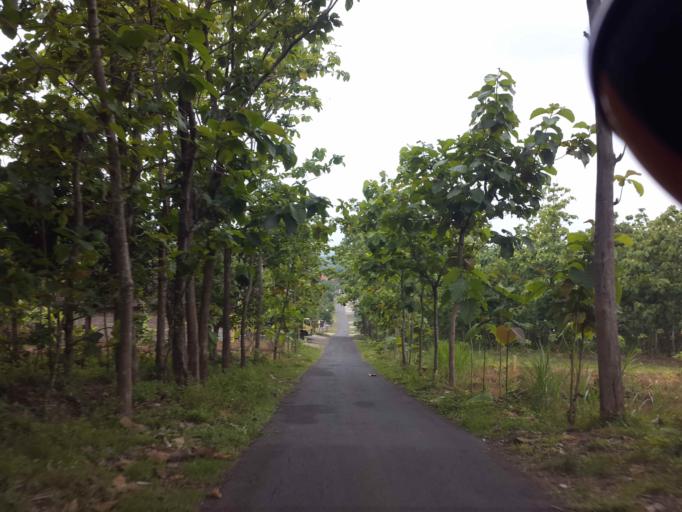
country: ID
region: East Java
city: Ponorogo
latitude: -7.7679
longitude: 111.3413
